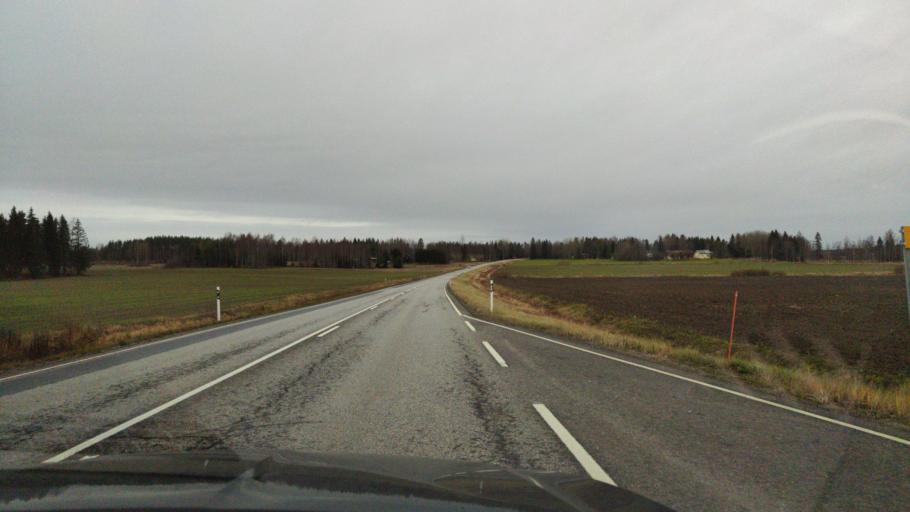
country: FI
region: Varsinais-Suomi
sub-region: Loimaa
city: Ylaene
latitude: 60.8576
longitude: 22.4215
